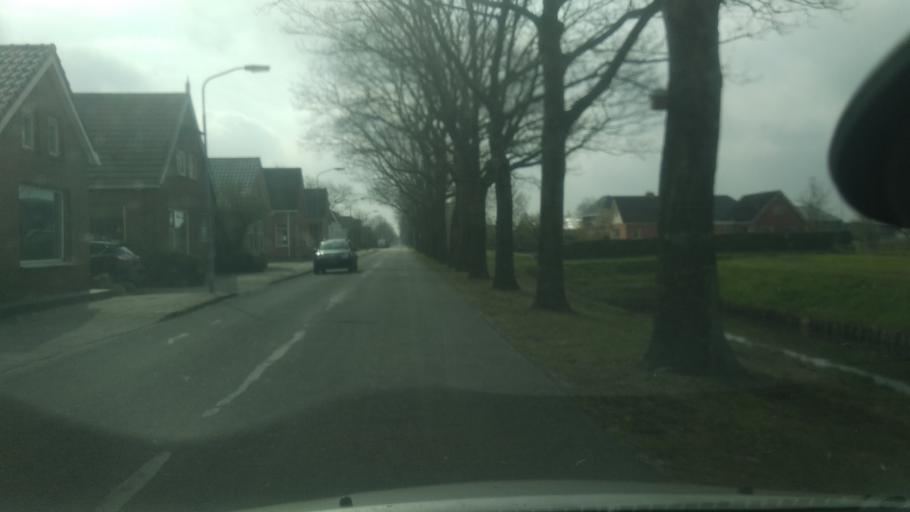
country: NL
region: Groningen
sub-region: Gemeente Stadskanaal
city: Stadskanaal
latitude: 52.9024
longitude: 6.9156
